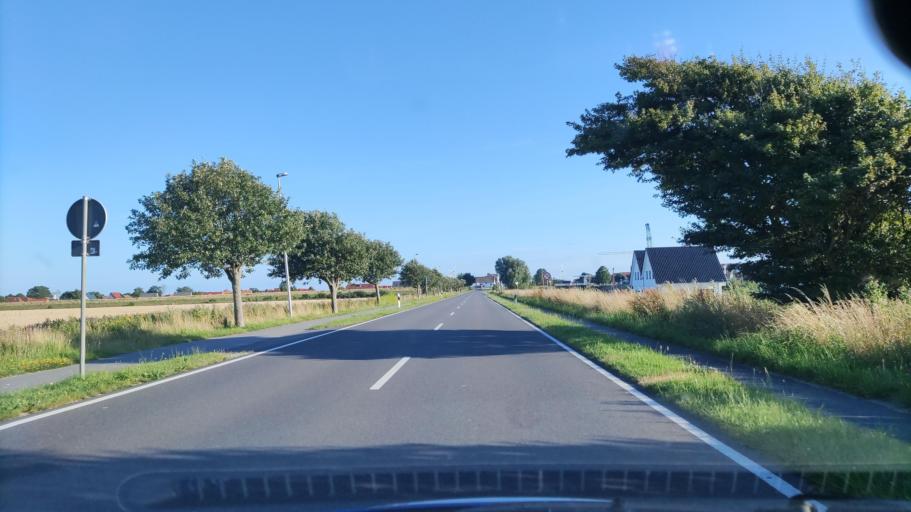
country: DE
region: Lower Saxony
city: Werdum
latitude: 53.7021
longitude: 7.8101
